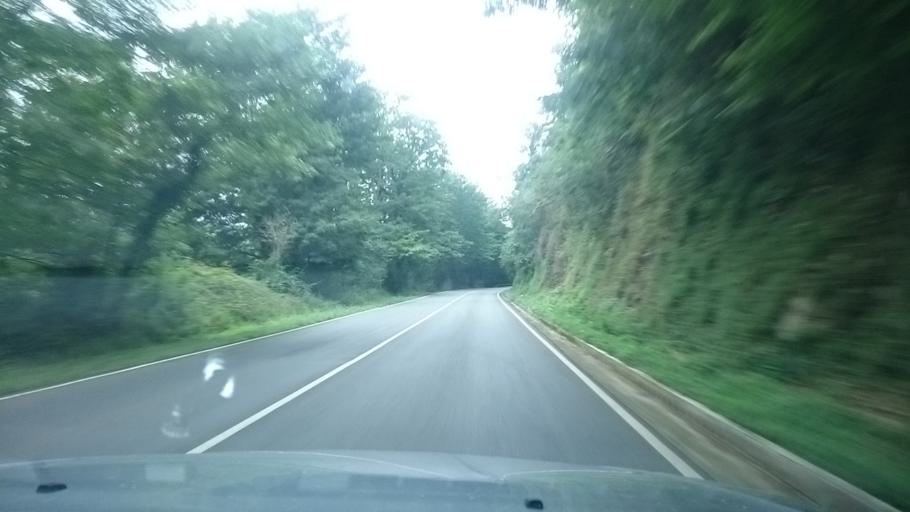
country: ES
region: Asturias
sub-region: Province of Asturias
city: Carrena
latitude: 43.4065
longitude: -4.8899
